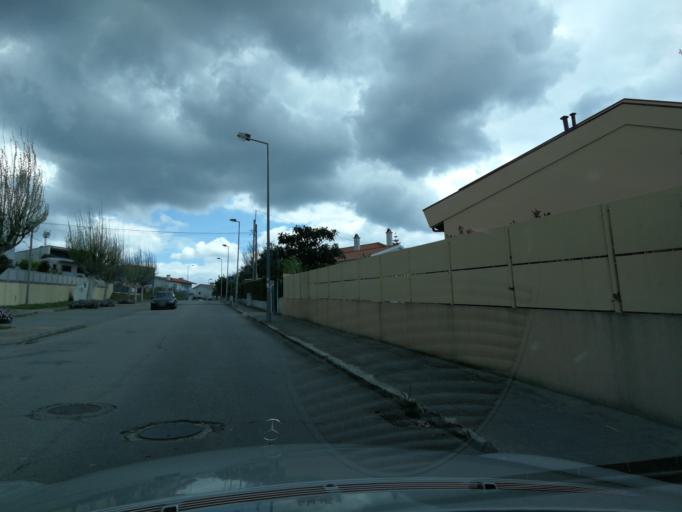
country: PT
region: Braga
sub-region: Braga
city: Braga
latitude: 41.5334
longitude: -8.4151
